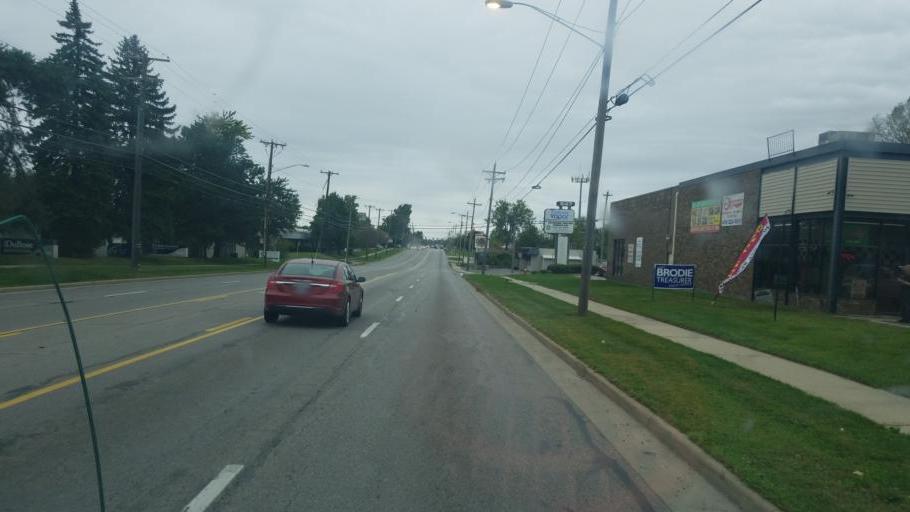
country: US
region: Ohio
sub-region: Lucas County
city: Ottawa Hills
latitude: 41.6332
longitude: -83.6644
